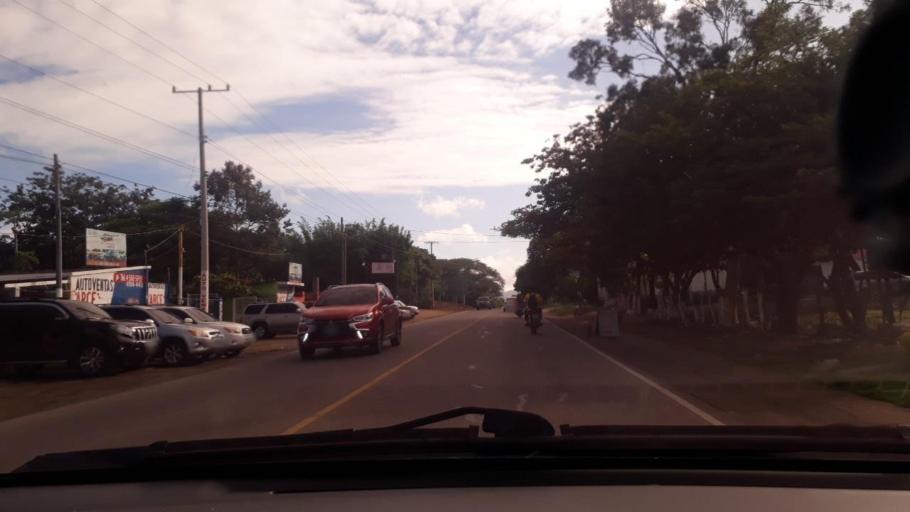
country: GT
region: Jutiapa
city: El Progreso
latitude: 14.3292
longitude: -89.8590
